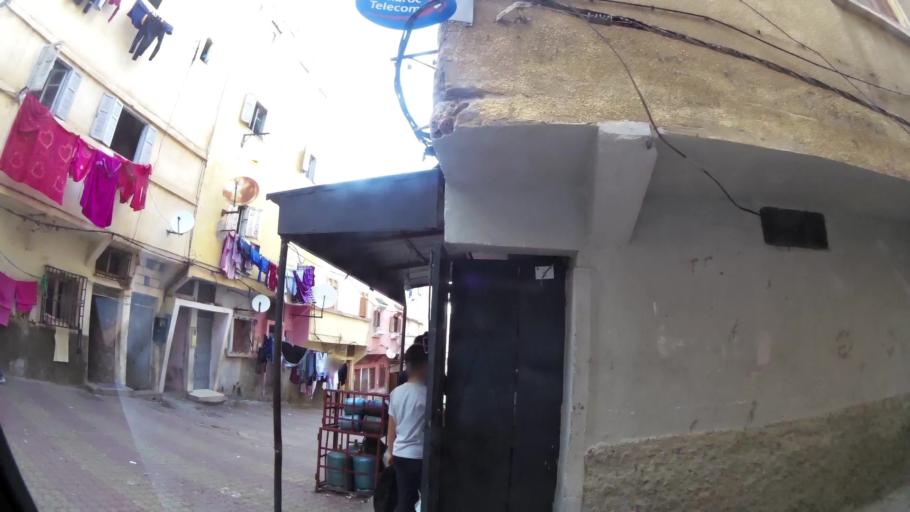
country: MA
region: Chaouia-Ouardigha
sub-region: Settat Province
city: Settat
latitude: 33.0068
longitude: -7.6277
